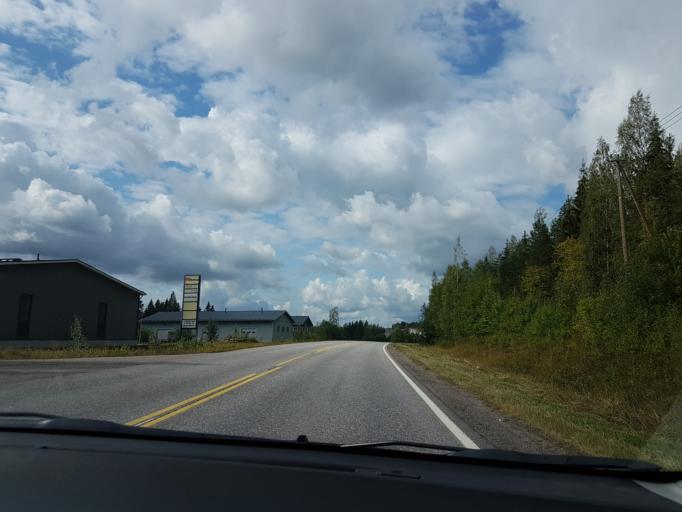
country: FI
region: Uusimaa
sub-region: Helsinki
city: Pornainen
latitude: 60.4753
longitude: 25.3162
